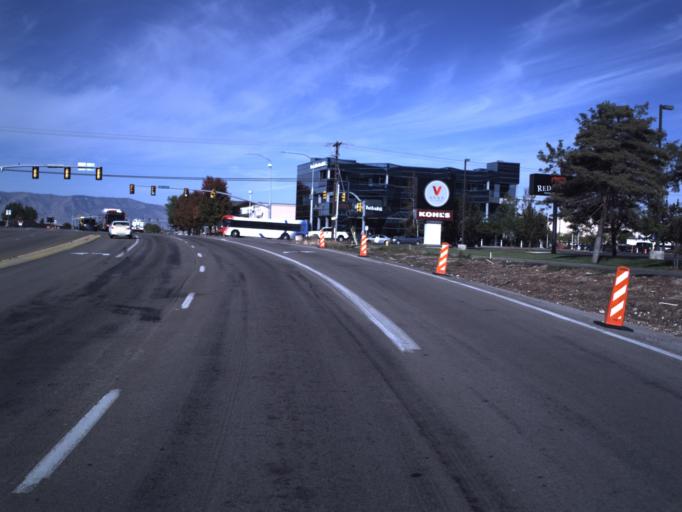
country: US
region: Utah
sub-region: Utah County
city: Orem
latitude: 40.2729
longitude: -111.6747
